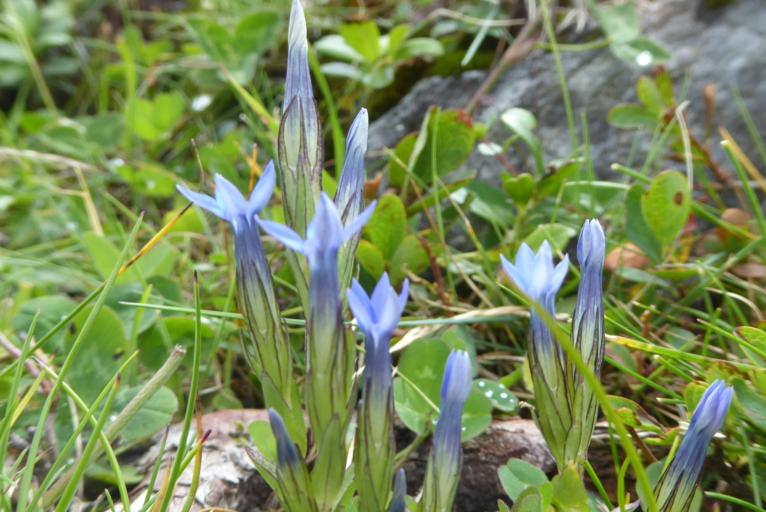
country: IT
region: Trentino-Alto Adige
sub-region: Bolzano
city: Predoi
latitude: 46.9763
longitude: 12.0905
